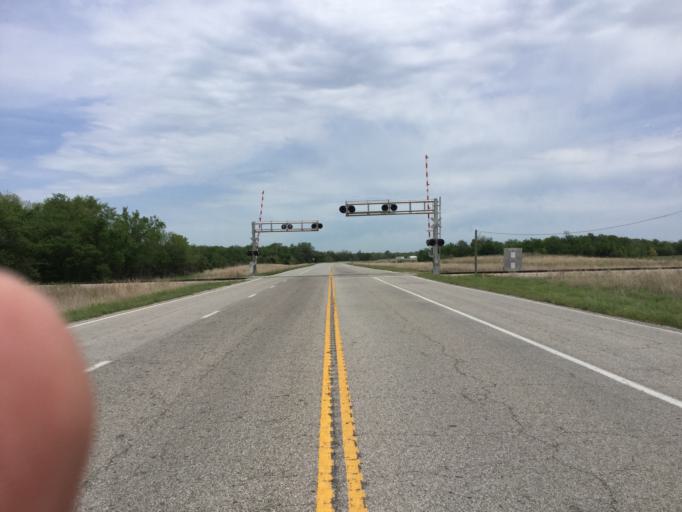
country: US
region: Kansas
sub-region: Montgomery County
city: Cherryvale
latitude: 37.2831
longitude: -95.5664
